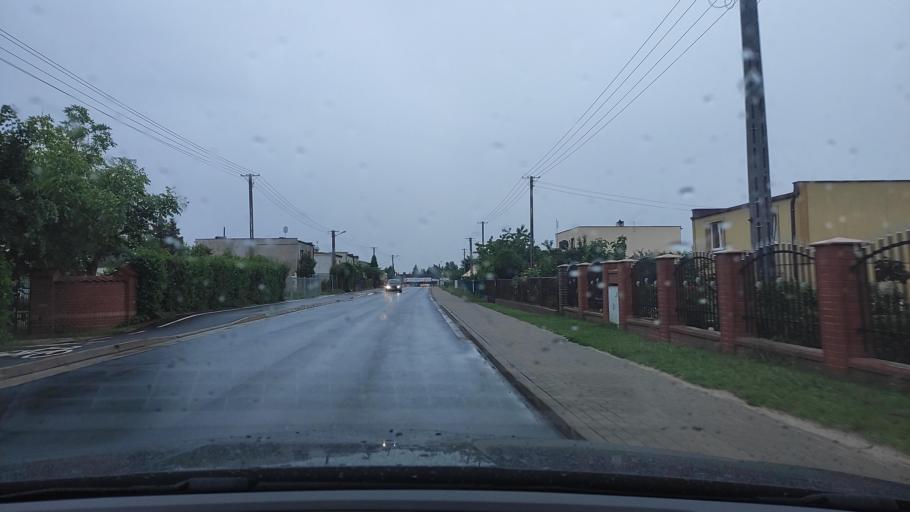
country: PL
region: Greater Poland Voivodeship
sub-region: Powiat poznanski
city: Kostrzyn
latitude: 52.4639
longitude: 17.1693
